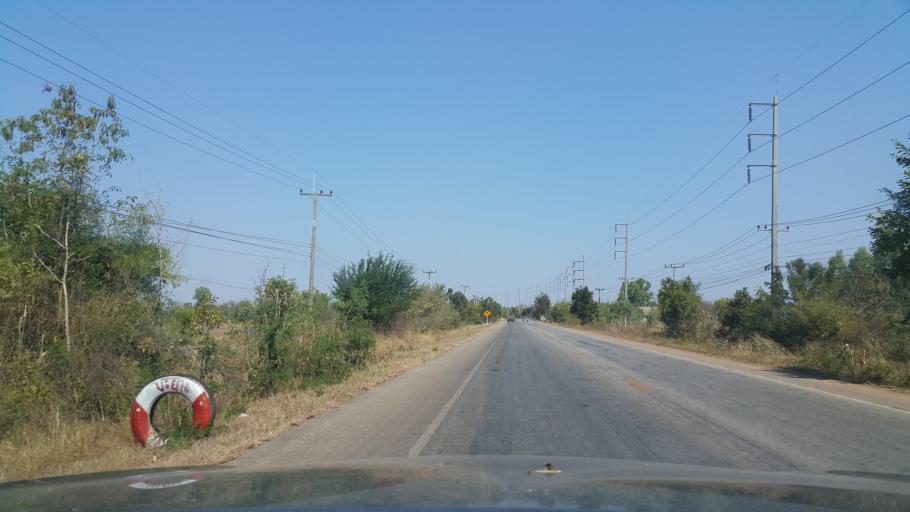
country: TH
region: Changwat Udon Thani
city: Thung Fon
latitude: 17.4653
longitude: 103.1912
